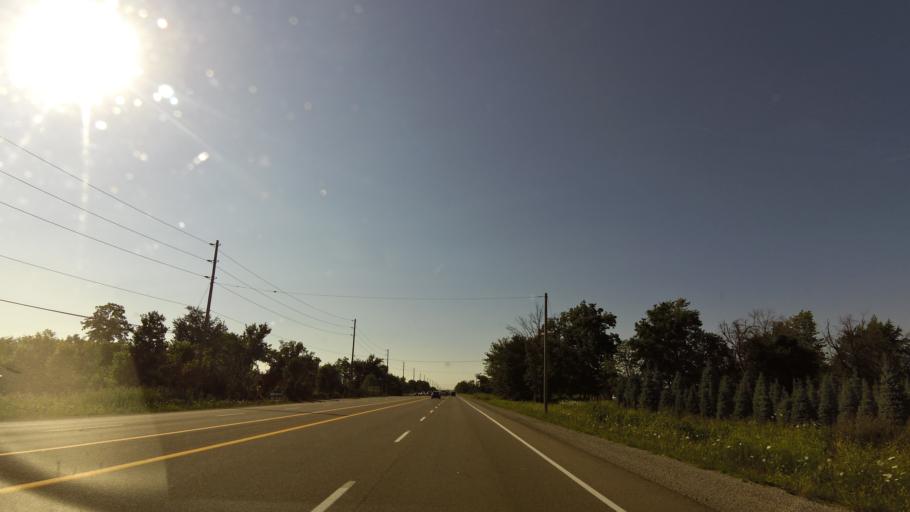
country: CA
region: Ontario
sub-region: Halton
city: Milton
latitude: 43.5481
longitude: -79.7983
